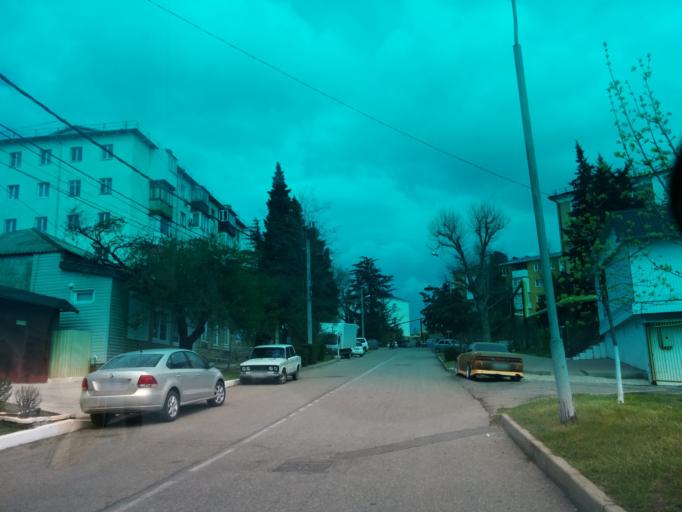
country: RU
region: Krasnodarskiy
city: Tuapse
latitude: 44.1043
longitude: 39.0833
